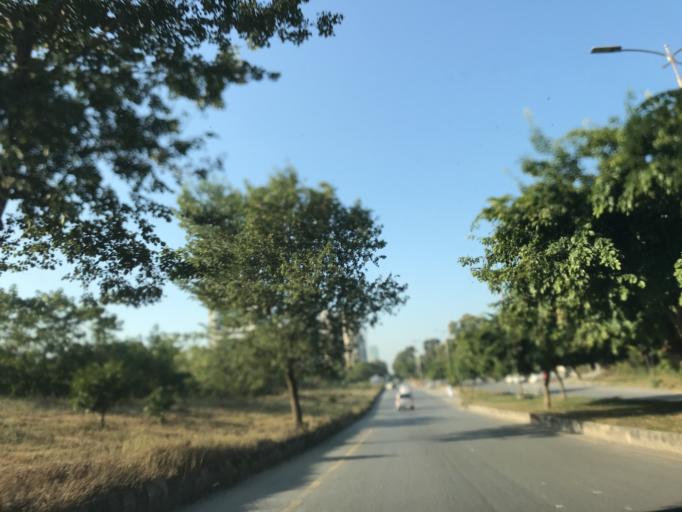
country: PK
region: Islamabad
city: Islamabad
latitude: 33.7180
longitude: 73.0680
